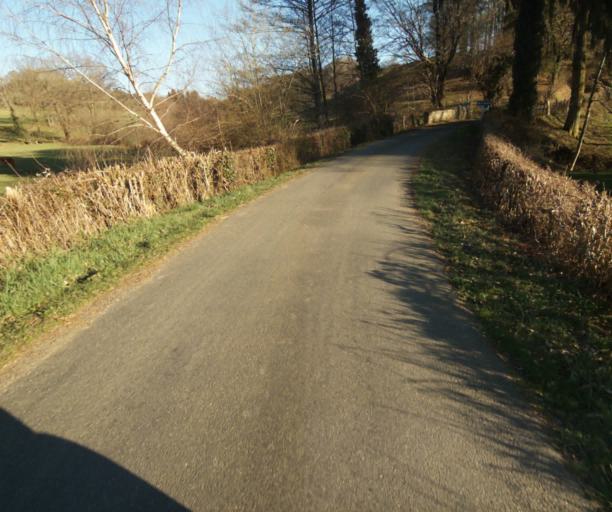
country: FR
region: Limousin
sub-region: Departement de la Correze
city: Saint-Clement
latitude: 45.3628
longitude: 1.6860
